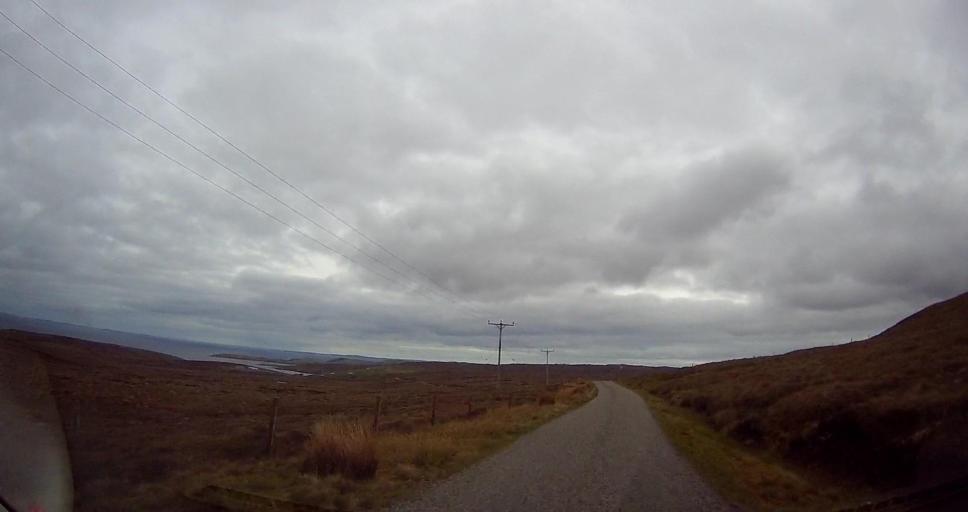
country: GB
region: Scotland
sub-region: Shetland Islands
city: Shetland
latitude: 60.5718
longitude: -1.0668
